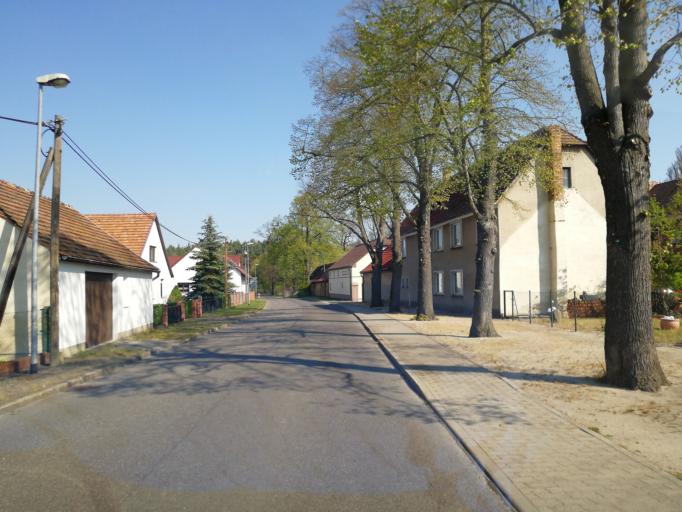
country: DE
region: Brandenburg
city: Bronkow
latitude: 51.7225
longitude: 13.8579
